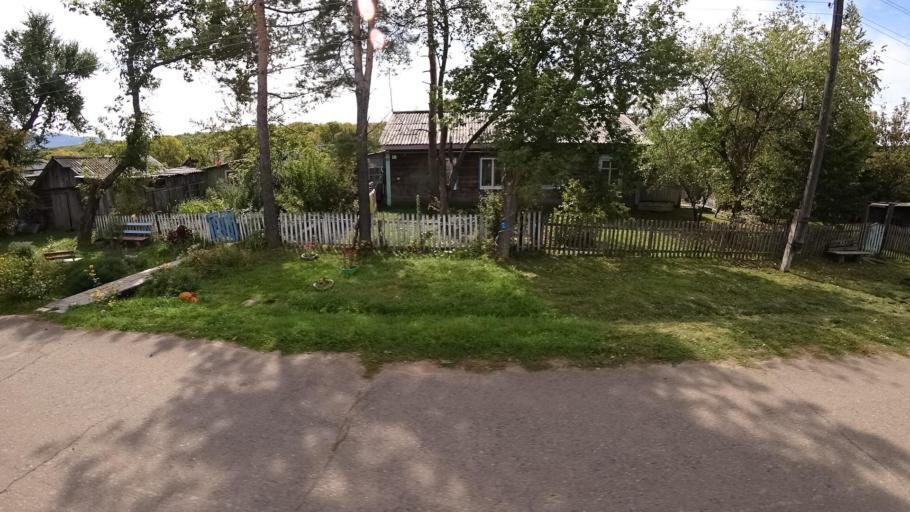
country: RU
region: Primorskiy
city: Yakovlevka
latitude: 44.6568
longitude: 133.7407
